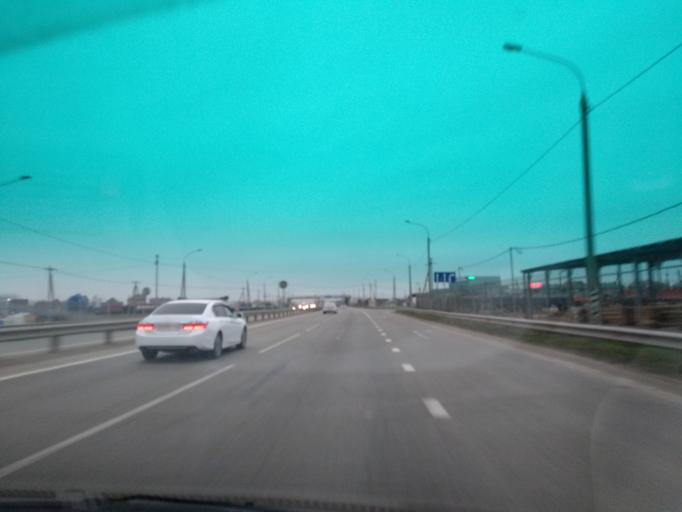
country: RU
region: Krasnodarskiy
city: Pashkovskiy
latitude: 45.0598
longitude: 39.1329
